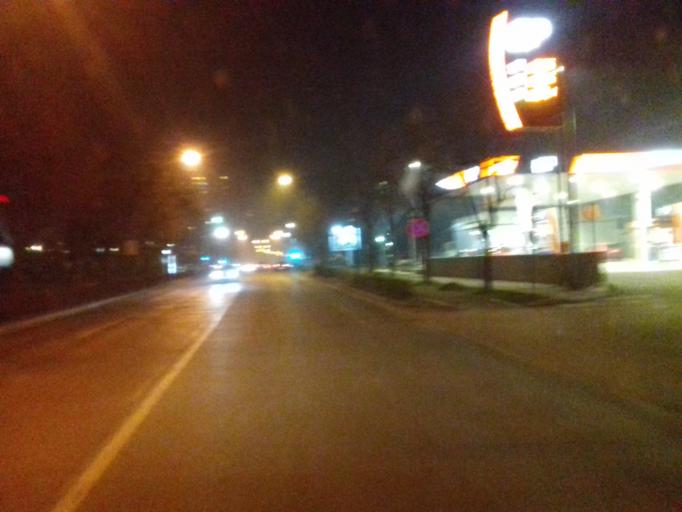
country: BA
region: Federation of Bosnia and Herzegovina
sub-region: Kanton Sarajevo
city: Sarajevo
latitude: 43.8502
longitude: 18.3861
